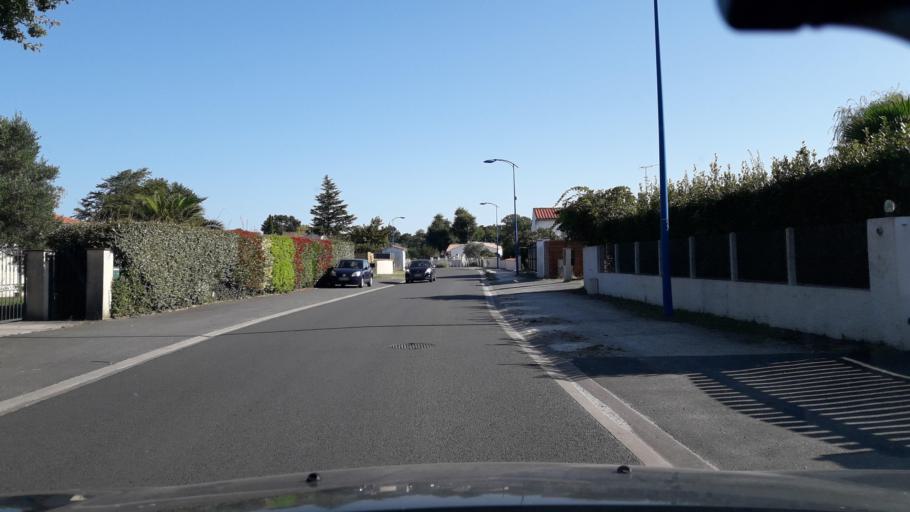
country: FR
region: Poitou-Charentes
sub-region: Departement de la Charente-Maritime
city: Etaules
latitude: 45.7258
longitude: -1.1008
